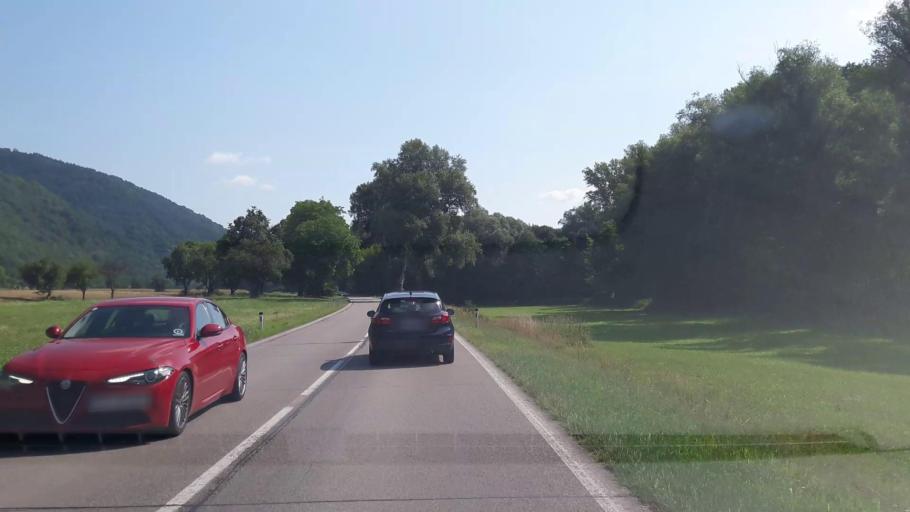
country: AT
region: Lower Austria
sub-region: Politischer Bezirk Melk
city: Emmersdorf an der Donau
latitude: 48.2627
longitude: 15.3676
